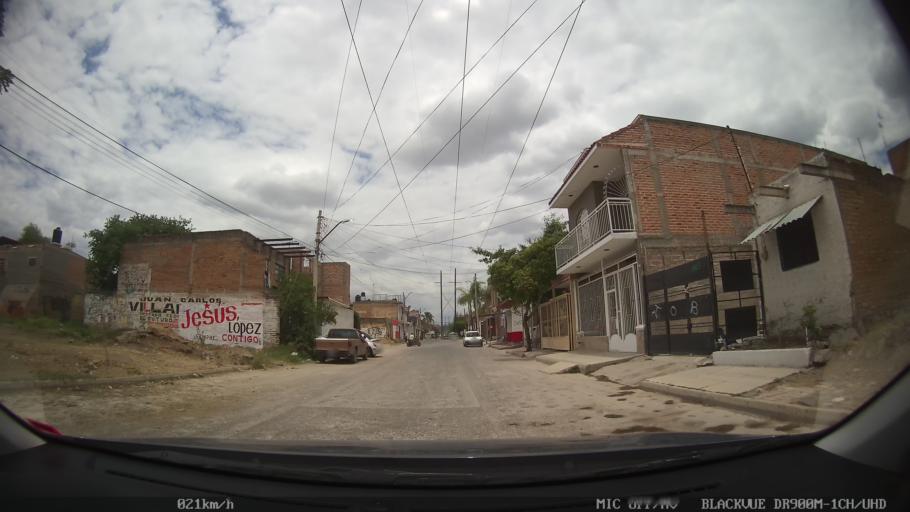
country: MX
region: Jalisco
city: Tlaquepaque
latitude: 20.6506
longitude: -103.2640
